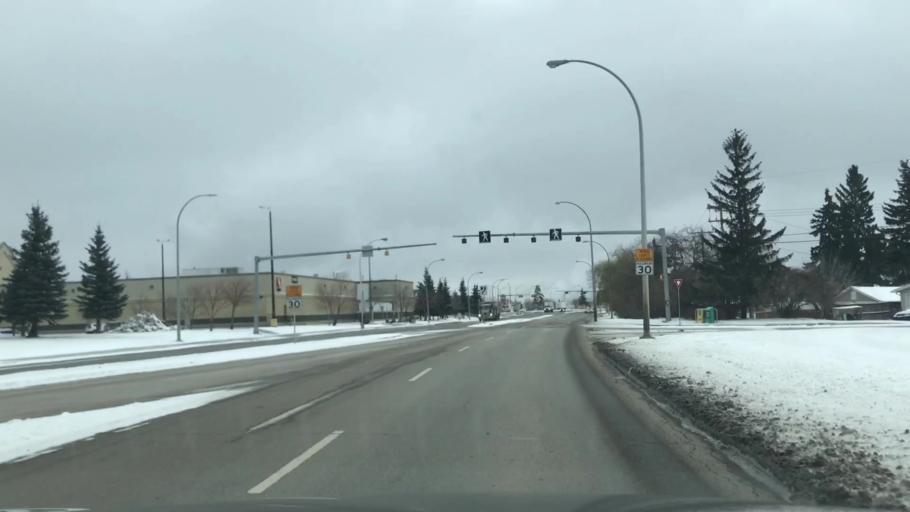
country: CA
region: Alberta
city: Edmonton
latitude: 53.5383
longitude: -113.4275
